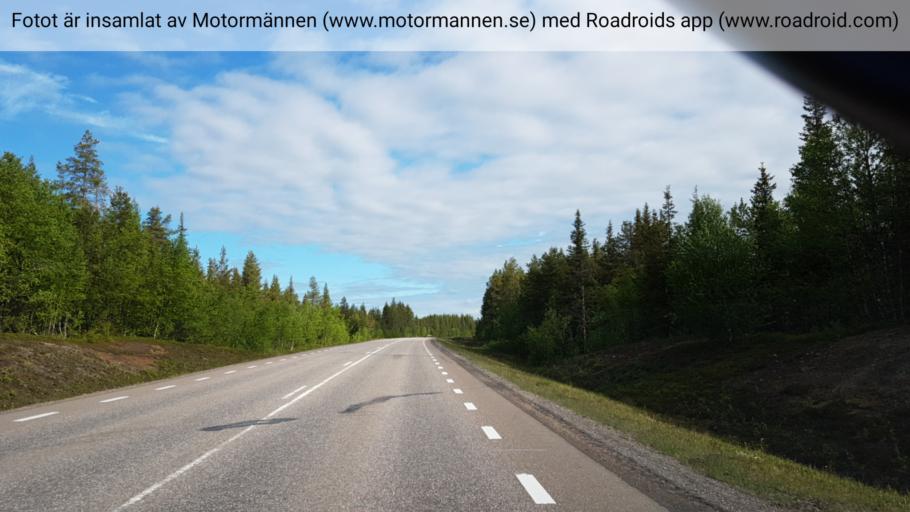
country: SE
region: Norrbotten
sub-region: Gallivare Kommun
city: Malmberget
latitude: 67.4818
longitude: 21.1240
